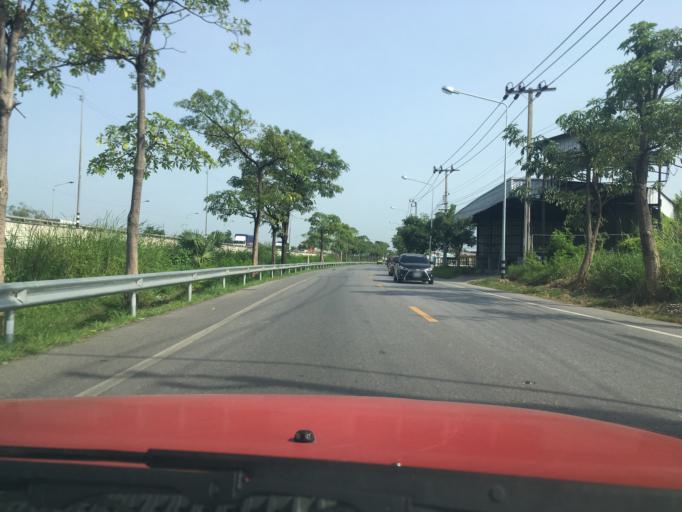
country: TH
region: Bangkok
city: Bang Khun Thian
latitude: 13.6305
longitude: 100.4181
